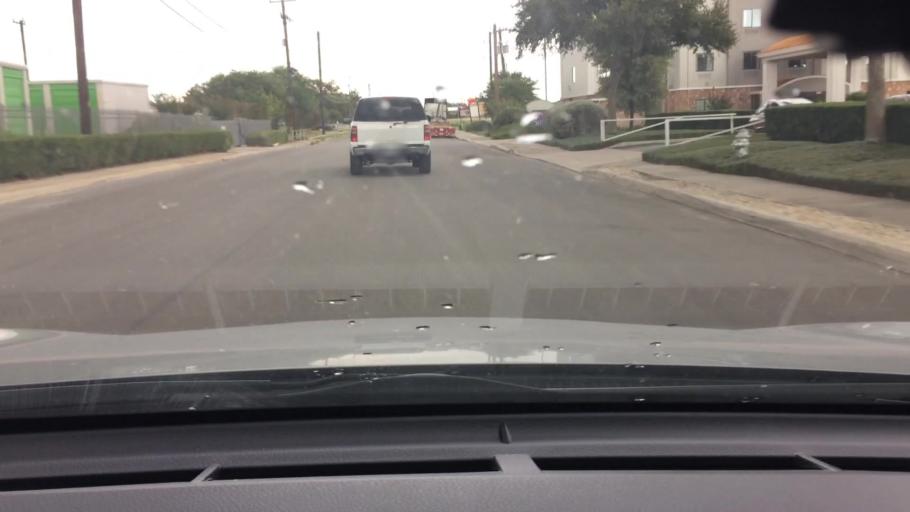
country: US
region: Texas
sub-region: Bexar County
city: Shavano Park
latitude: 29.5729
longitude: -98.5915
